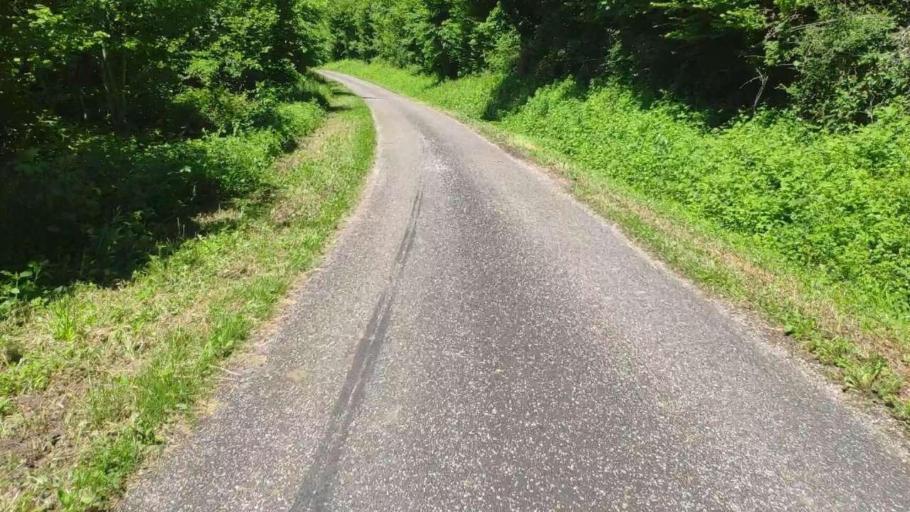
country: FR
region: Franche-Comte
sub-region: Departement du Jura
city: Perrigny
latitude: 46.7329
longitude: 5.6534
